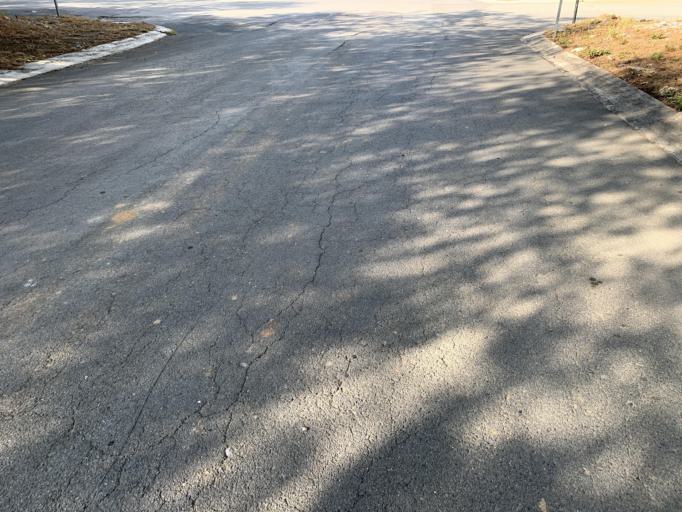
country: MX
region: Nuevo Leon
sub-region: Juarez
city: Bosques de San Pedro
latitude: 25.5133
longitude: -100.1893
